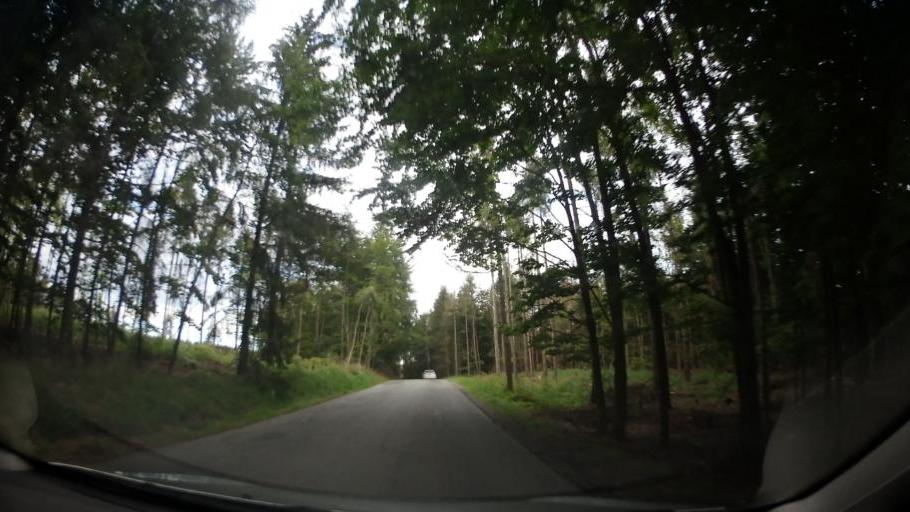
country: CZ
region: Olomoucky
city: Horni Stepanov
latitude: 49.5394
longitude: 16.7289
